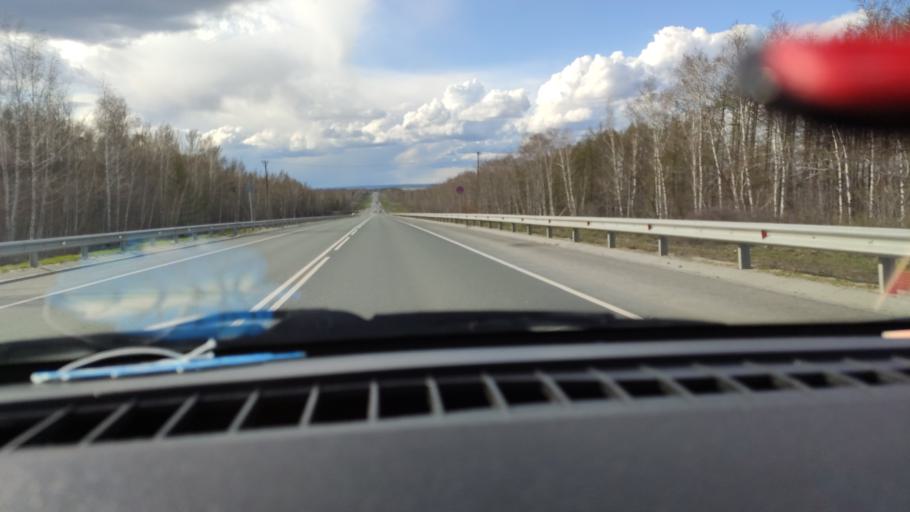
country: RU
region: Saratov
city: Shikhany
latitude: 52.1507
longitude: 47.1883
